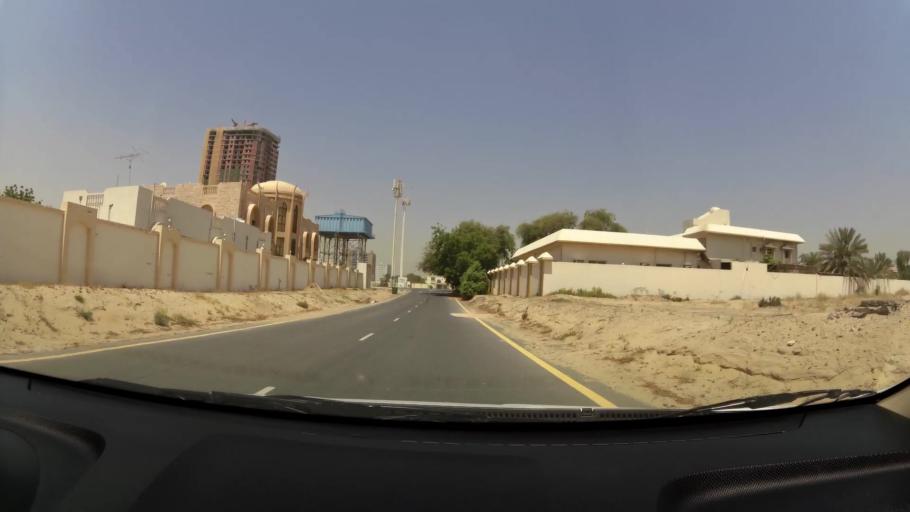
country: AE
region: Ajman
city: Ajman
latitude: 25.3995
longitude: 55.5150
